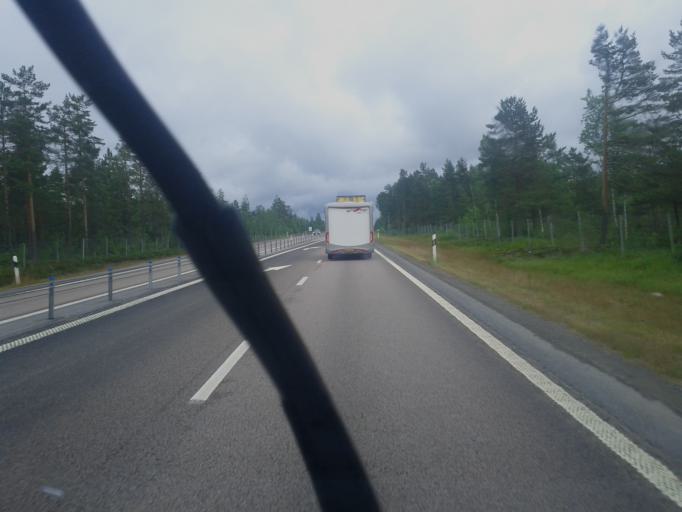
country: SE
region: Vaesternorrland
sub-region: Haernoesands Kommun
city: Haernoesand
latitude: 62.5665
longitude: 17.7347
